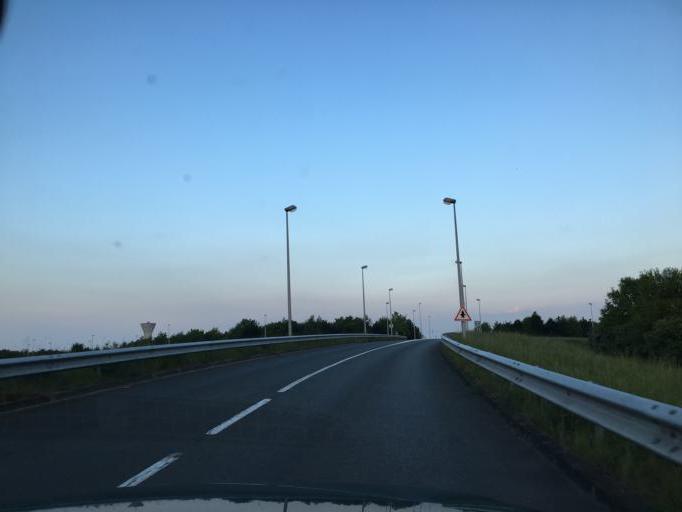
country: FR
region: Centre
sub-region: Departement du Loiret
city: Saint-Jean-de-la-Ruelle
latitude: 47.9281
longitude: 1.8724
